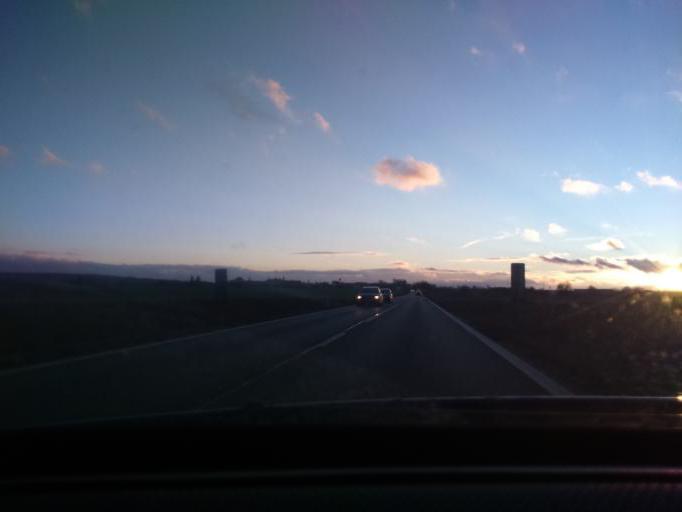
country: CZ
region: Plzensky
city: Chotesov
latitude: 49.6656
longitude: 13.2070
